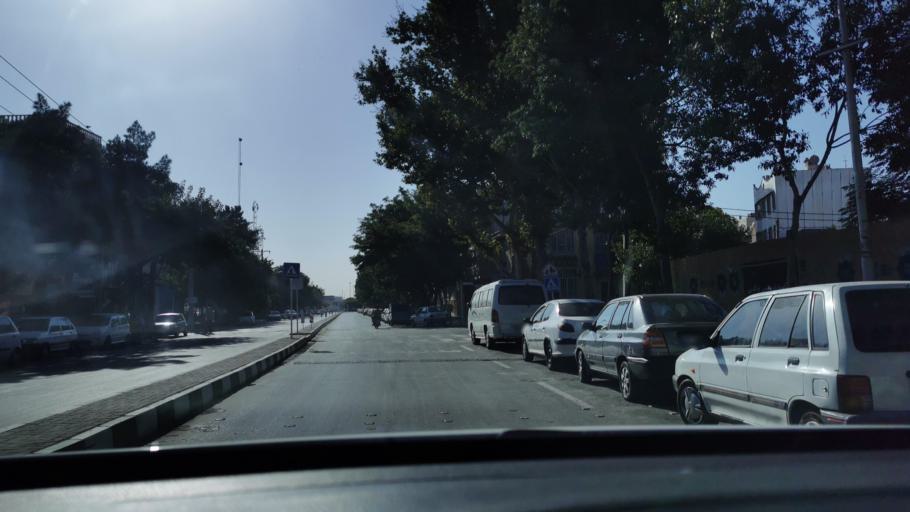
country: IR
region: Razavi Khorasan
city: Mashhad
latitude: 36.2968
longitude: 59.6234
